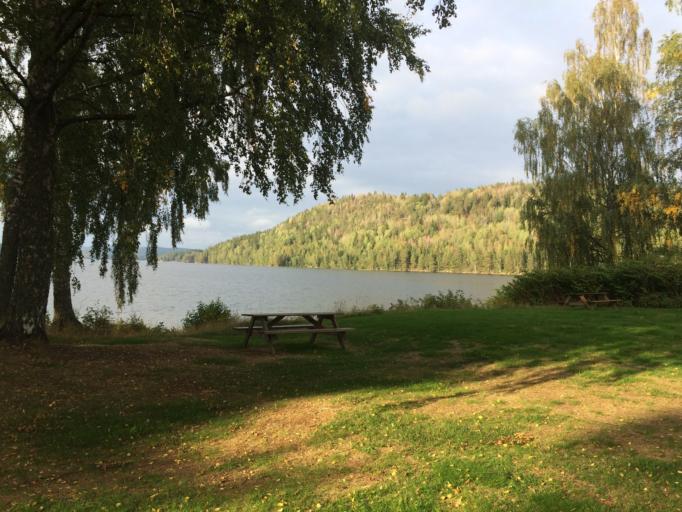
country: SE
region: Vaestra Goetaland
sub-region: Bengtsfors Kommun
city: Dals Langed
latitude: 58.9999
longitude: 12.4621
